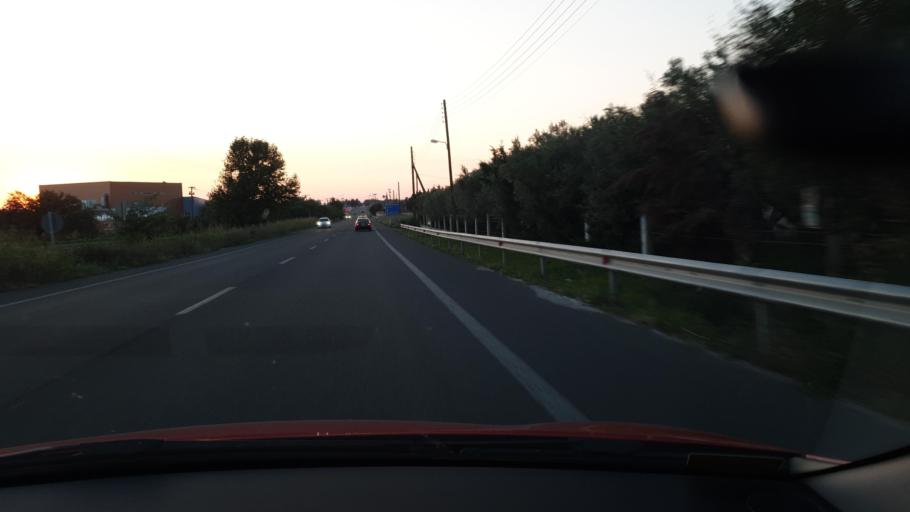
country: GR
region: Central Macedonia
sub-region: Nomos Thessalonikis
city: Agia Paraskevi
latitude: 40.5153
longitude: 23.0710
